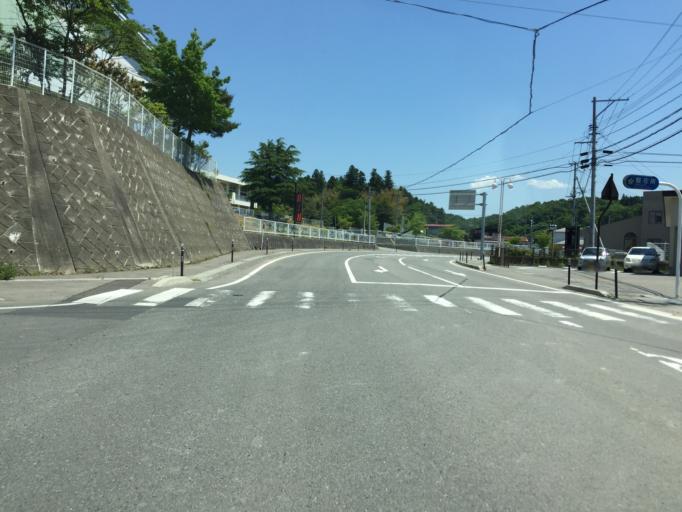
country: JP
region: Fukushima
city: Miharu
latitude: 37.5020
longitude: 140.4731
